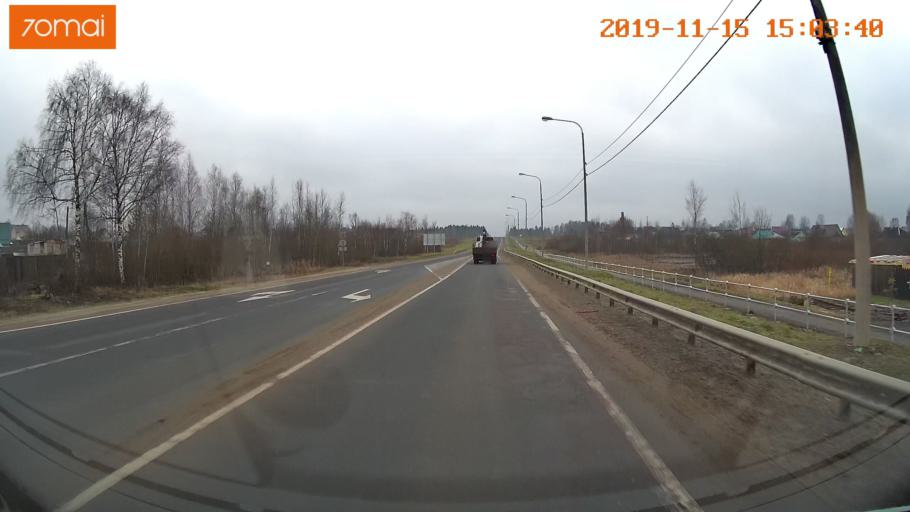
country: RU
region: Jaroslavl
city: Prechistoye
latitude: 58.4225
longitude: 40.3247
